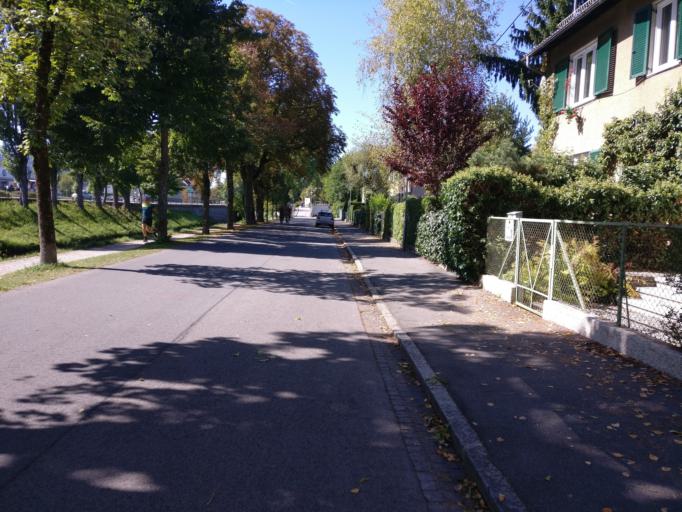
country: AT
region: Carinthia
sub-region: Klagenfurt am Woerthersee
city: Klagenfurt am Woerthersee
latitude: 46.6200
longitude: 14.2729
